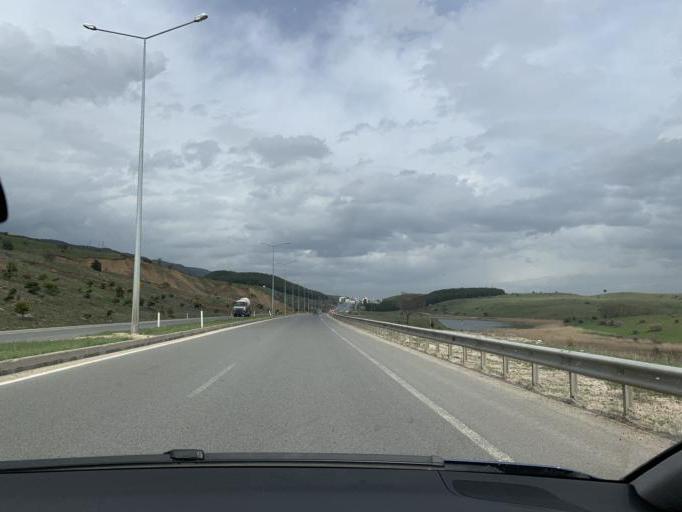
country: TR
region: Bolu
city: Gerede
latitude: 40.7974
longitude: 32.1611
